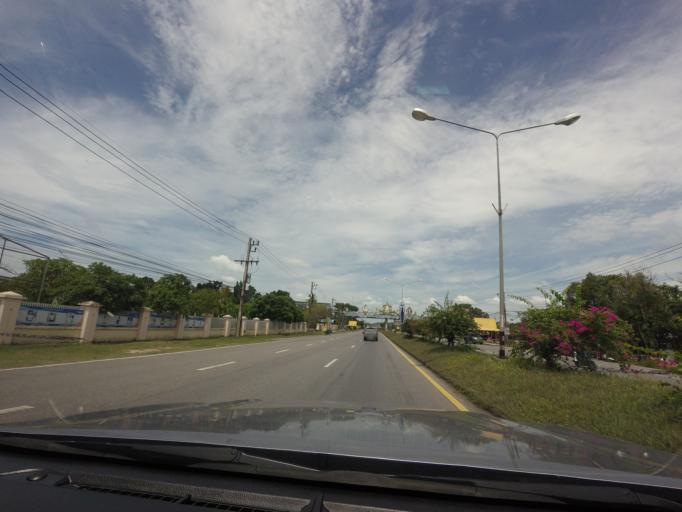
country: TH
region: Songkhla
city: Singhanakhon
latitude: 7.2401
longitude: 100.5472
